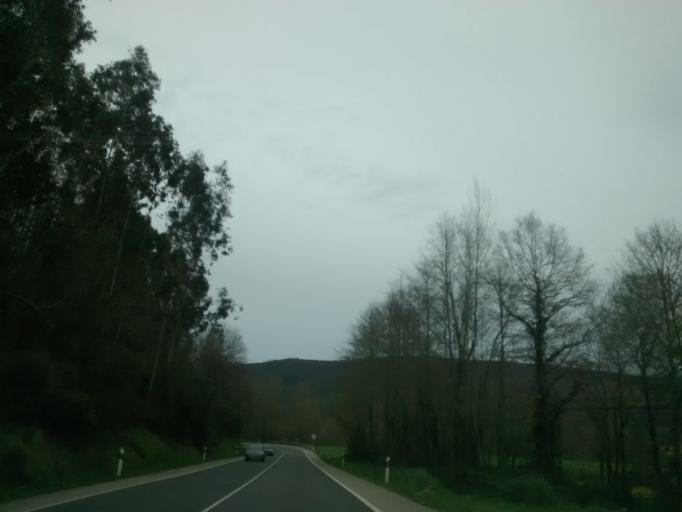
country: ES
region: Cantabria
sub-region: Provincia de Cantabria
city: Puente Viesgo
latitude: 43.3108
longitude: -3.9595
